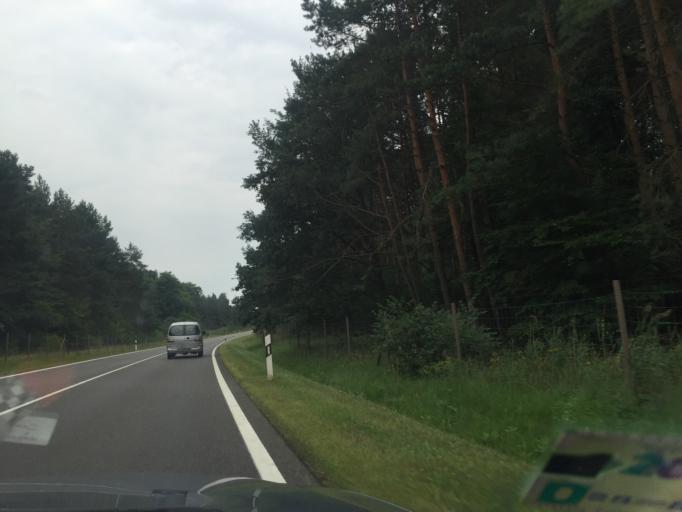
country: DE
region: Brandenburg
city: Wandlitz
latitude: 52.7295
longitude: 13.5314
